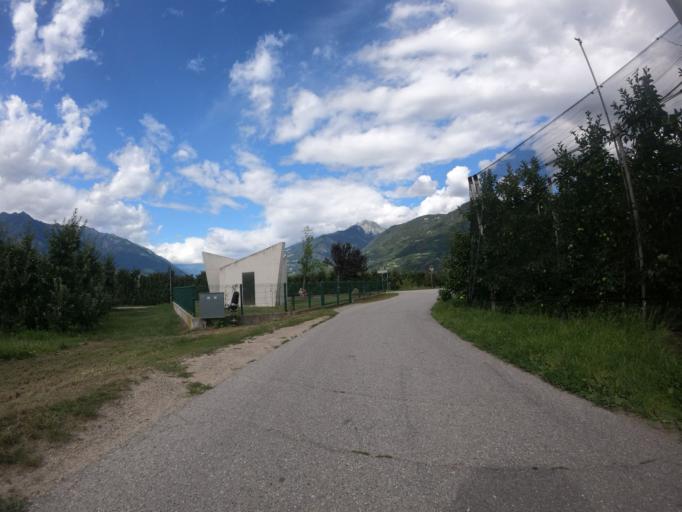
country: IT
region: Trentino-Alto Adige
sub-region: Bolzano
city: Cermes
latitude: 46.6299
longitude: 11.1518
